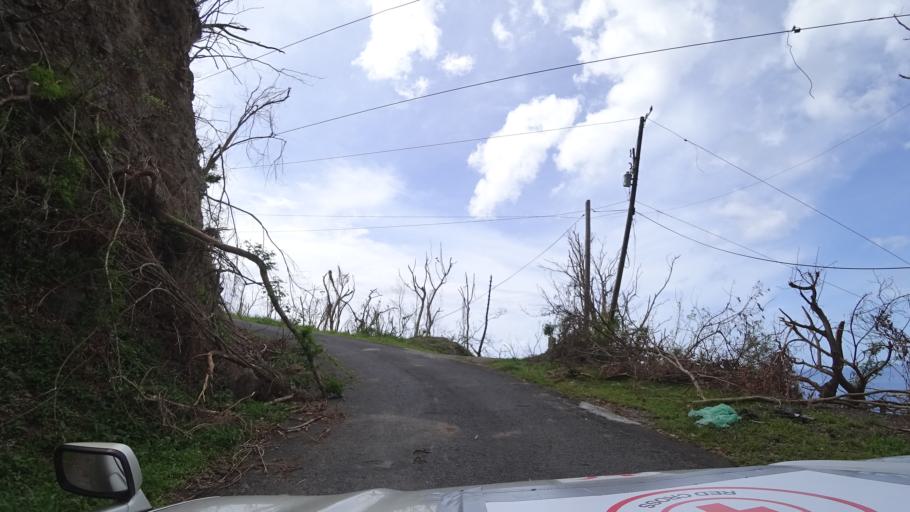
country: DM
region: Saint Mark
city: Soufriere
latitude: 15.2423
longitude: -61.3682
